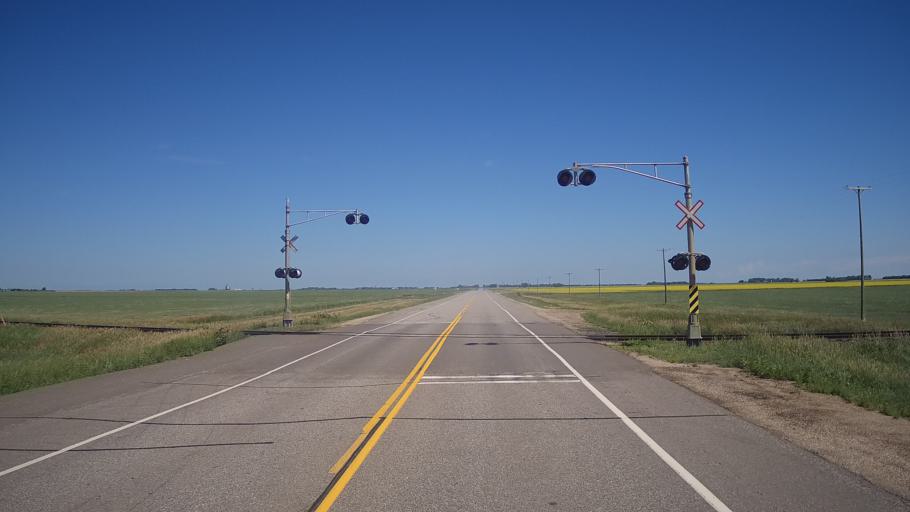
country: CA
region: Manitoba
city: Portage la Prairie
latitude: 50.0089
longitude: -98.4688
